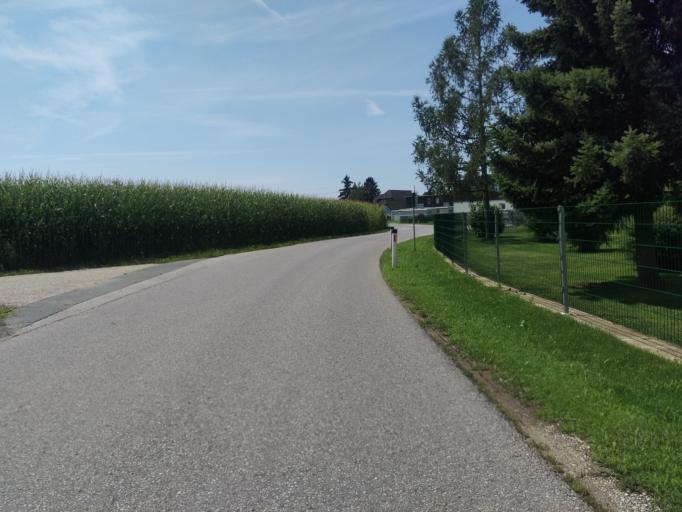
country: AT
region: Styria
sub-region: Politischer Bezirk Graz-Umgebung
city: Unterpremstatten
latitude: 46.9794
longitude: 15.4095
